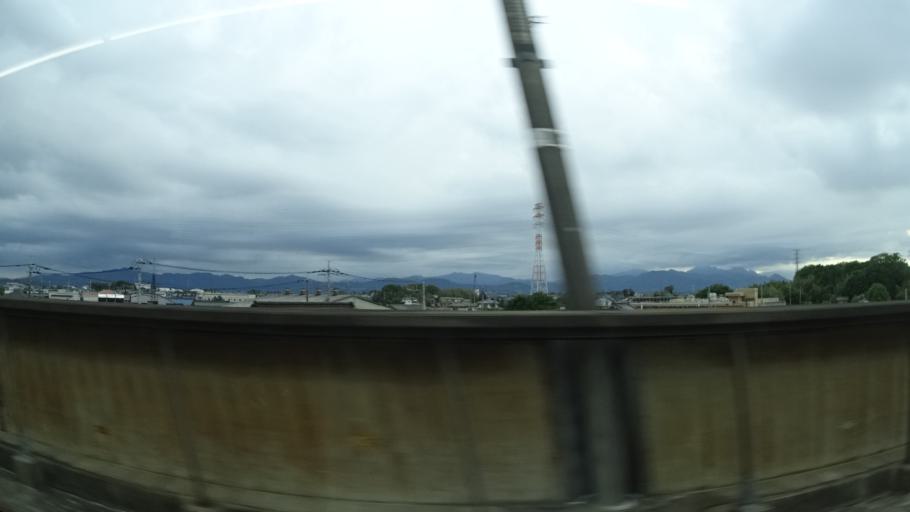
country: JP
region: Saitama
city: Kodamacho-kodamaminami
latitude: 36.2430
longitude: 139.1305
